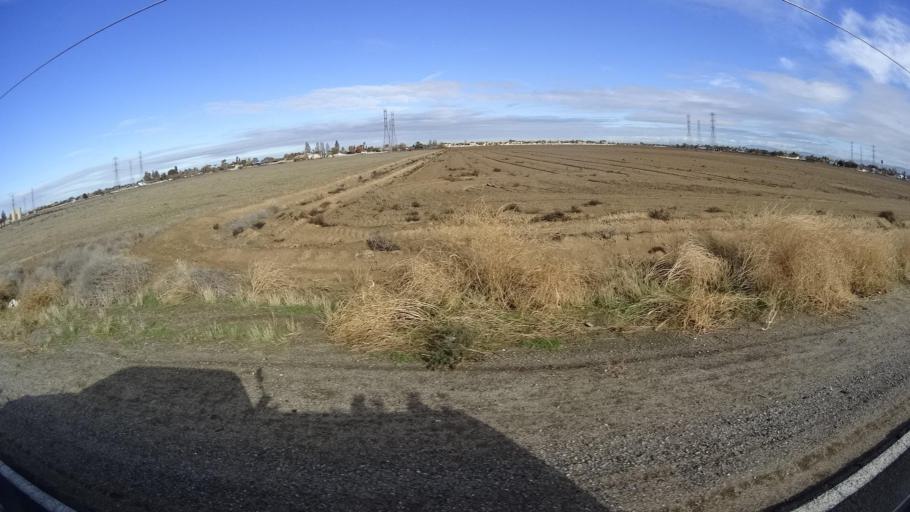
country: US
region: California
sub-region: Kern County
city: Rosedale
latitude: 35.3834
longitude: -119.1765
